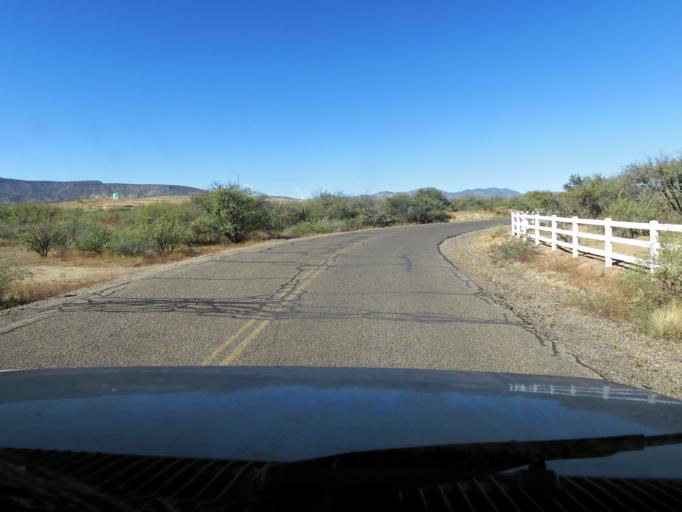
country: US
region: Arizona
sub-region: Yavapai County
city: Camp Verde
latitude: 34.5985
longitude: -111.8934
